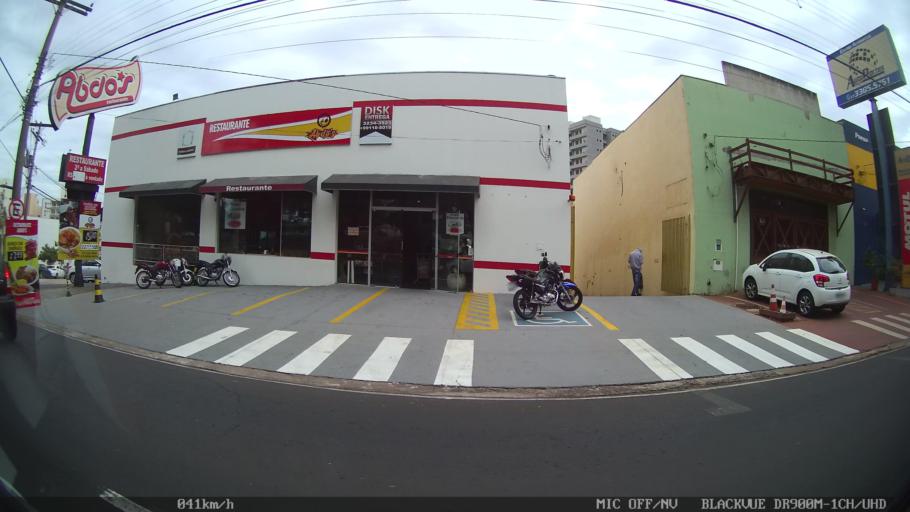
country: BR
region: Sao Paulo
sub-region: Sao Jose Do Rio Preto
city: Sao Jose do Rio Preto
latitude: -20.8230
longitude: -49.3970
